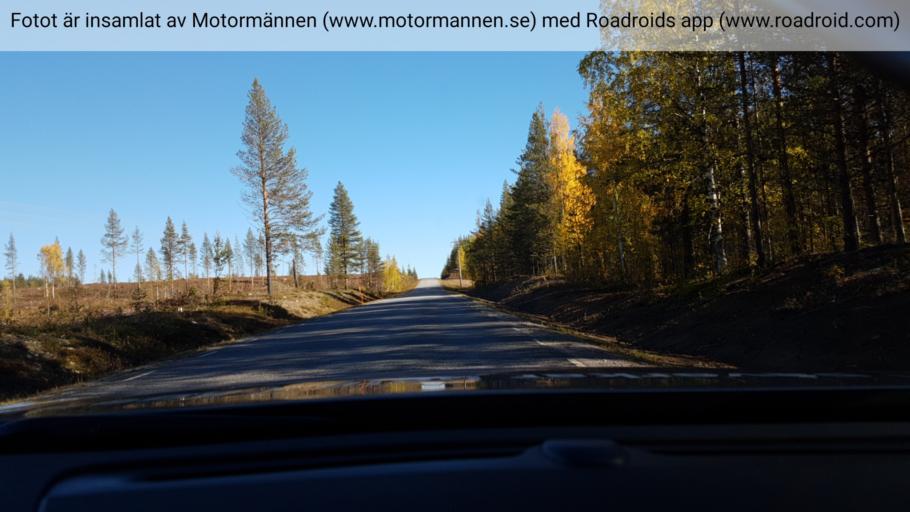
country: SE
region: Norrbotten
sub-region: Gallivare Kommun
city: Gaellivare
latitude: 66.4689
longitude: 20.8392
